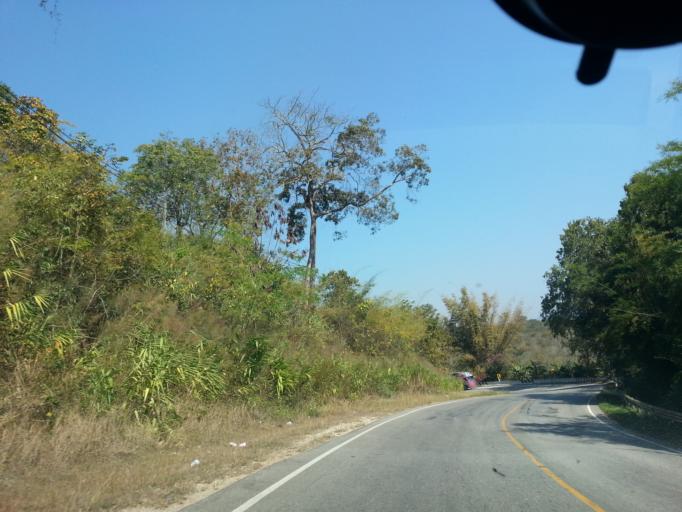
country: TH
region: Chiang Mai
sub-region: Amphoe Chiang Dao
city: Chiang Dao
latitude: 19.4349
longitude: 98.9820
